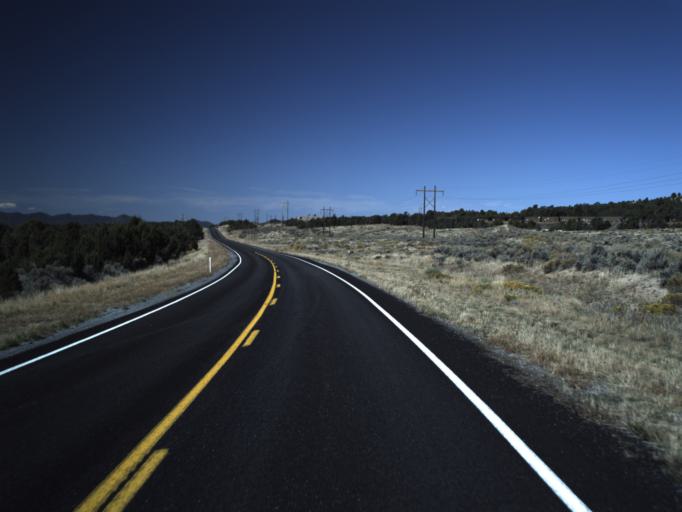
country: US
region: Utah
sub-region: Iron County
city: Cedar City
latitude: 37.6107
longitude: -113.3736
